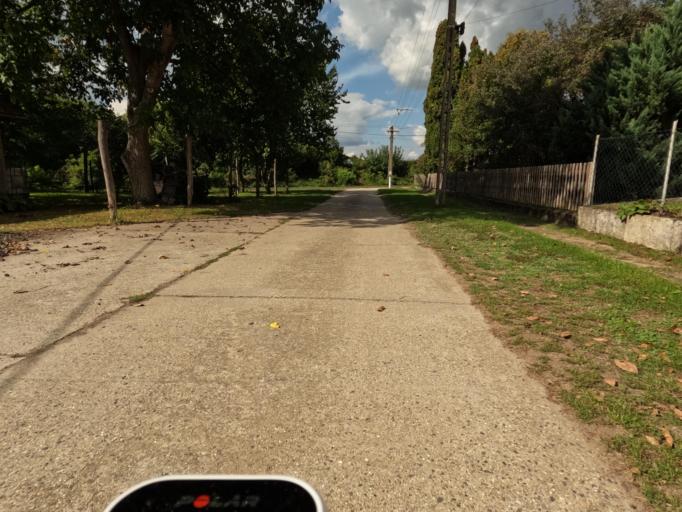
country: HU
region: Tolna
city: Tengelic
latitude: 46.5086
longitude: 18.6889
